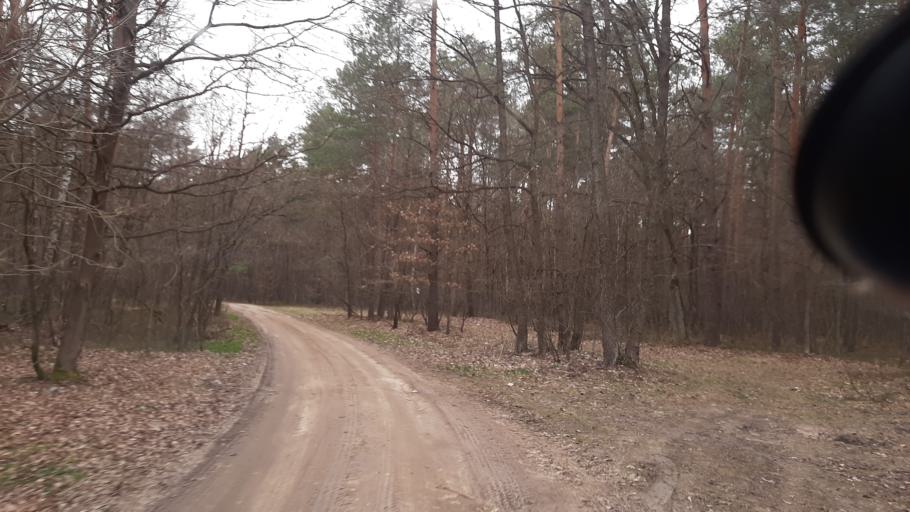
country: PL
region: Lublin Voivodeship
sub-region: Powiat lubartowski
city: Abramow
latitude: 51.4431
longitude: 22.3446
